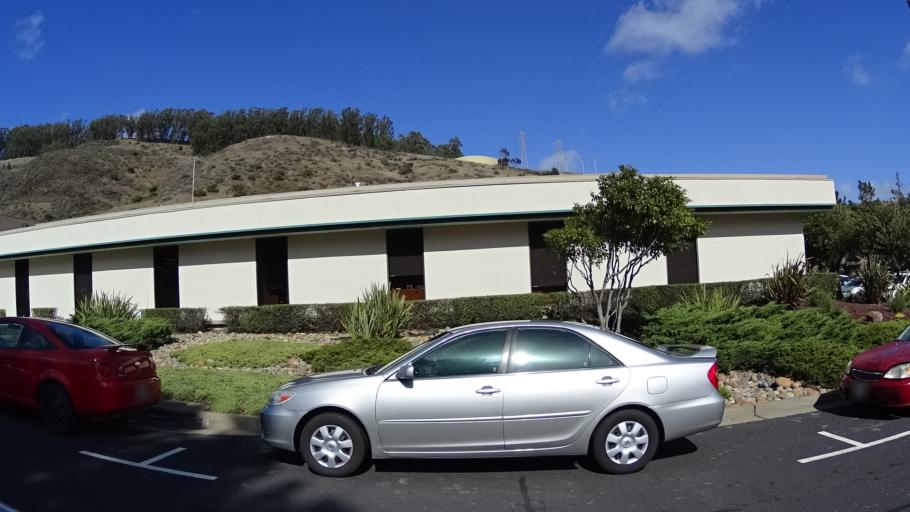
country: US
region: California
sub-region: San Mateo County
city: Brisbane
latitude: 37.6929
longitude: -122.4243
